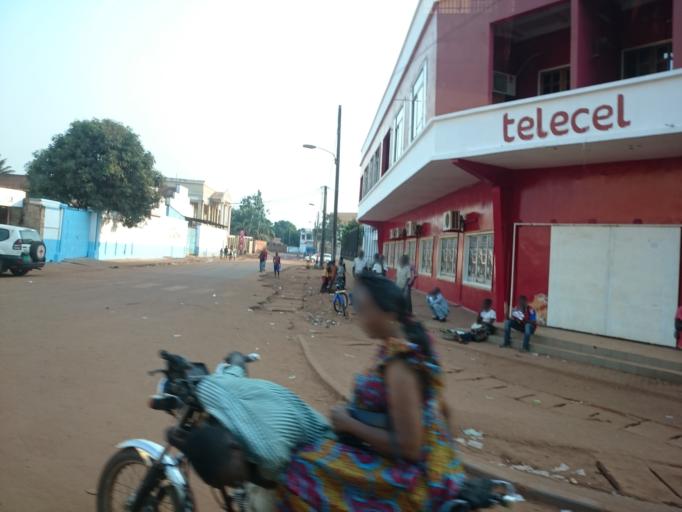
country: CF
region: Bangui
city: Bangui
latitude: 4.3627
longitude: 18.5791
